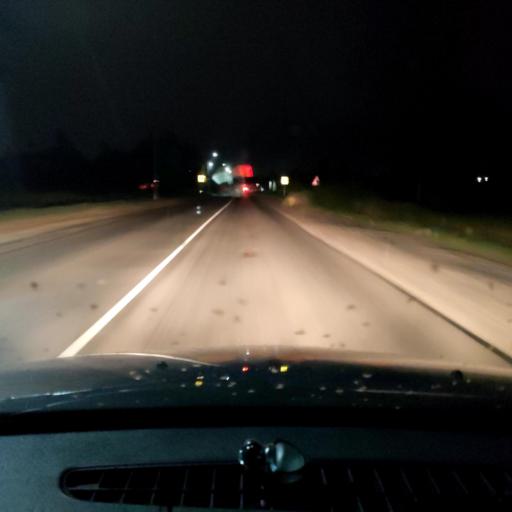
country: RU
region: Voronezj
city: Novaya Usman'
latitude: 51.6564
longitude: 39.4391
